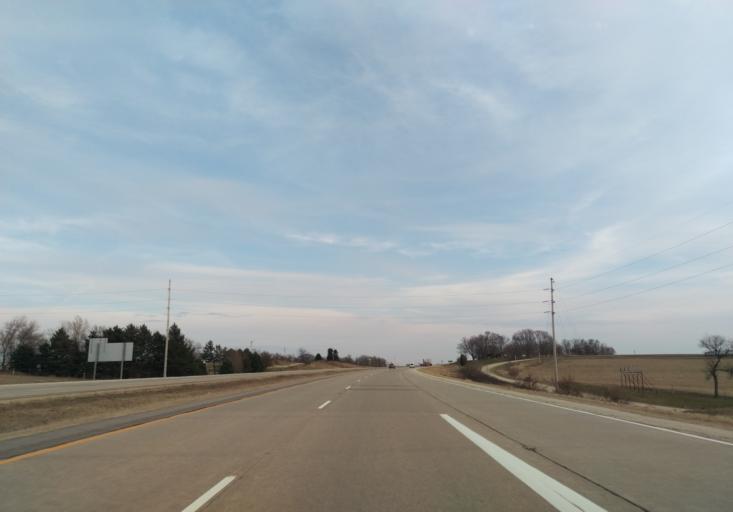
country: US
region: Wisconsin
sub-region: Dane County
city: Mount Horeb
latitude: 42.9969
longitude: -89.6646
